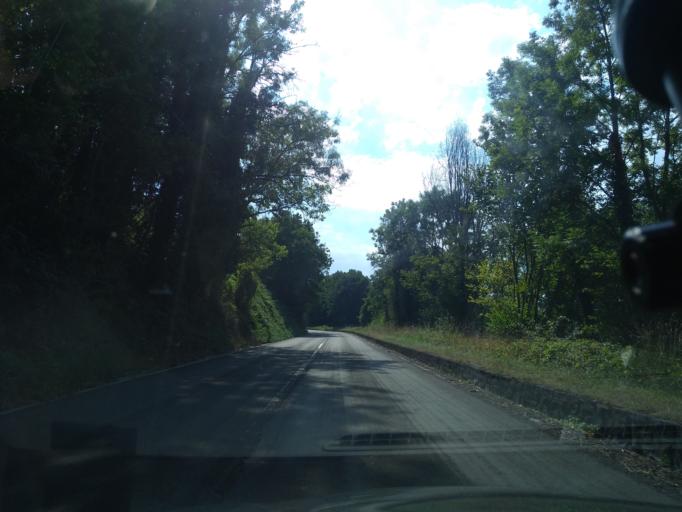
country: BE
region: Wallonia
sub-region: Province de Namur
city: Dinant
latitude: 50.2363
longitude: 4.8941
